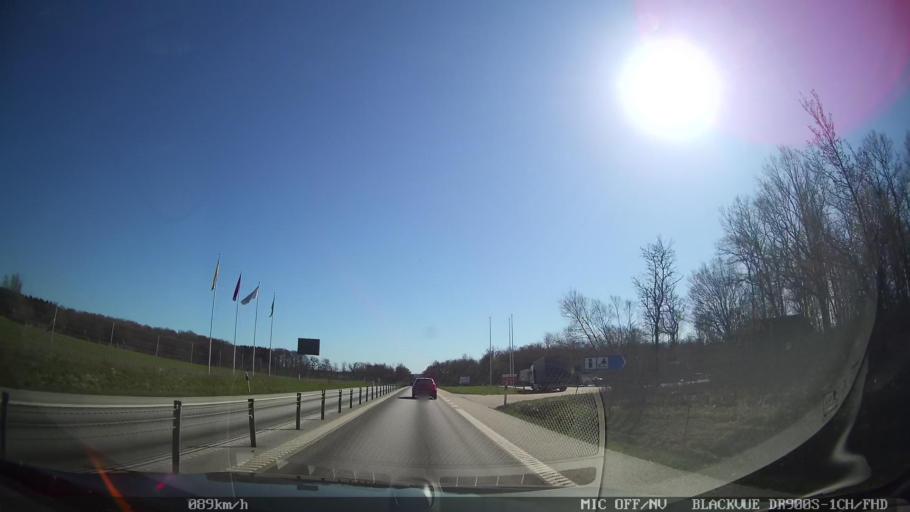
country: SE
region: Skane
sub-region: Svedala Kommun
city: Svedala
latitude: 55.5118
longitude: 13.3079
